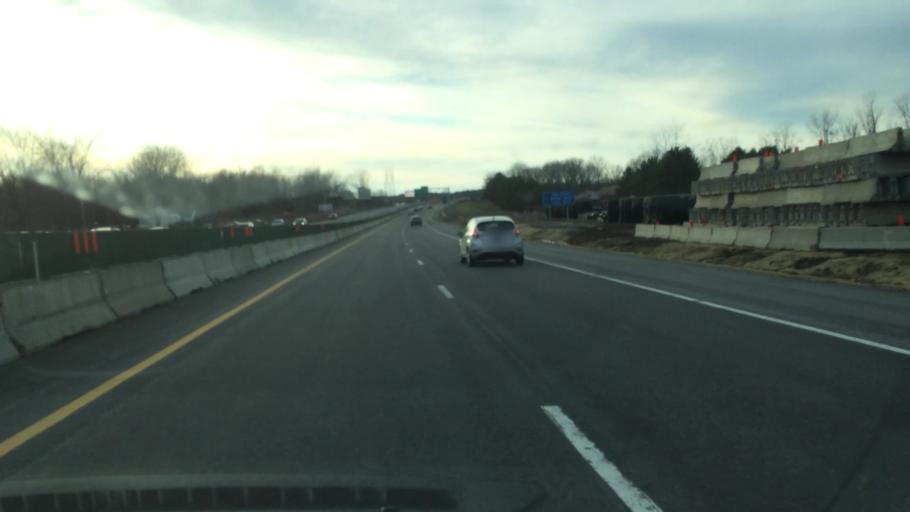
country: US
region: Ohio
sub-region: Summit County
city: Barberton
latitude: 41.0393
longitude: -81.5970
